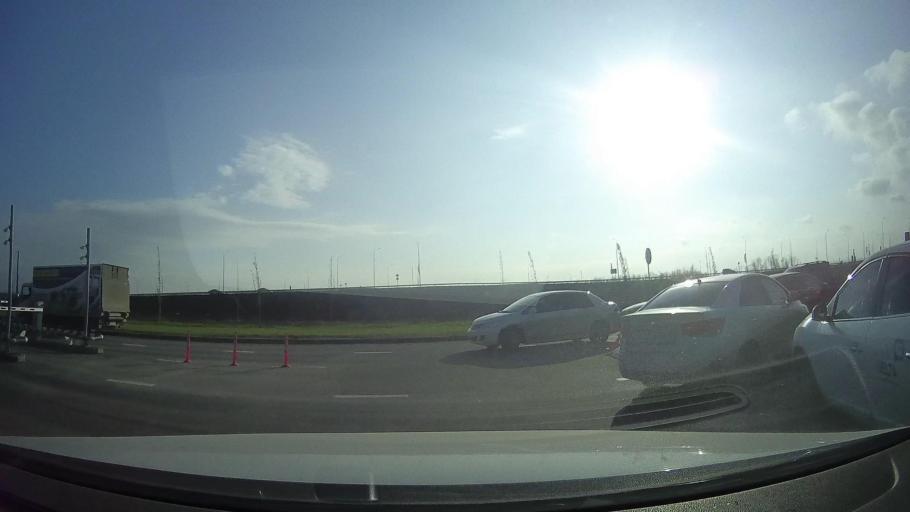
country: RU
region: Rostov
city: Grushevskaya
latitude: 47.4876
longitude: 39.9346
